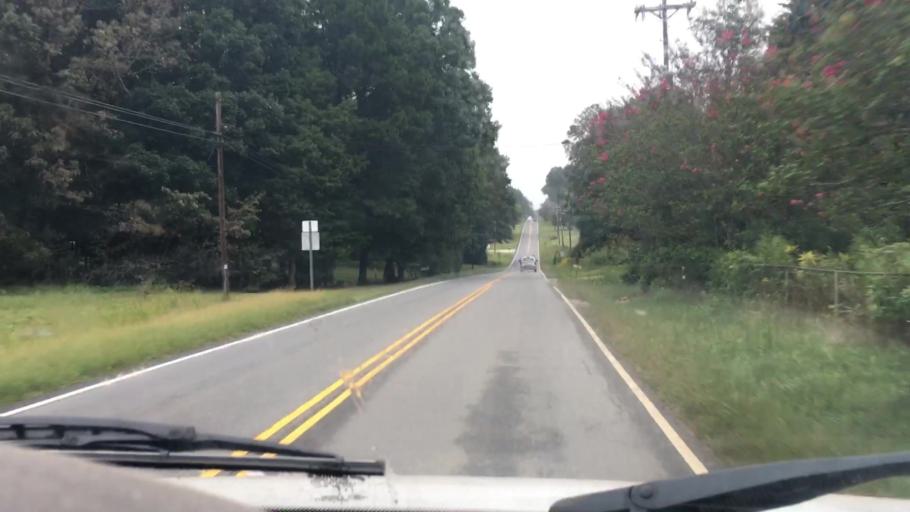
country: US
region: North Carolina
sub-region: Iredell County
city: Mooresville
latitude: 35.6094
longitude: -80.7917
